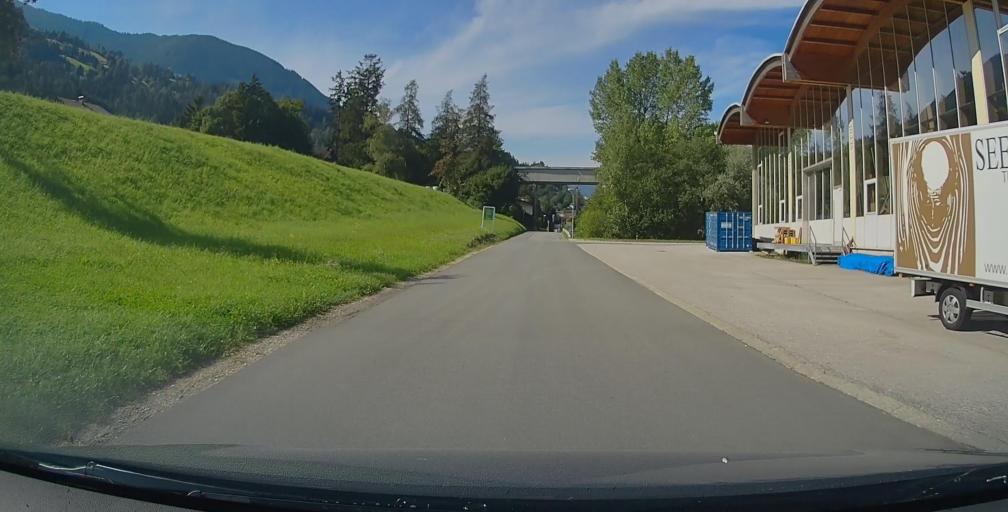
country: AT
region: Tyrol
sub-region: Politischer Bezirk Schwaz
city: Stans
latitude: 47.3563
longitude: 11.7302
